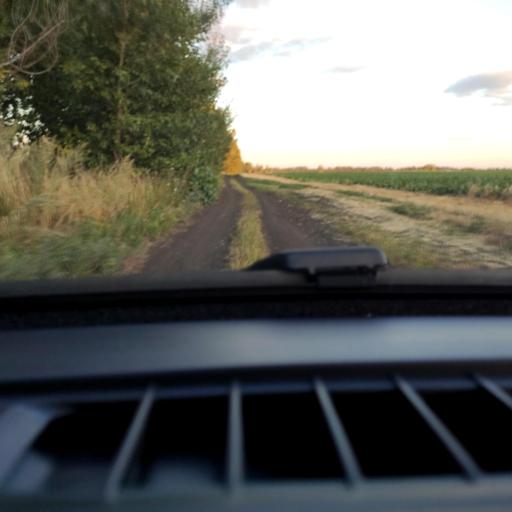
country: RU
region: Voronezj
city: Panino
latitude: 51.5766
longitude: 39.8762
